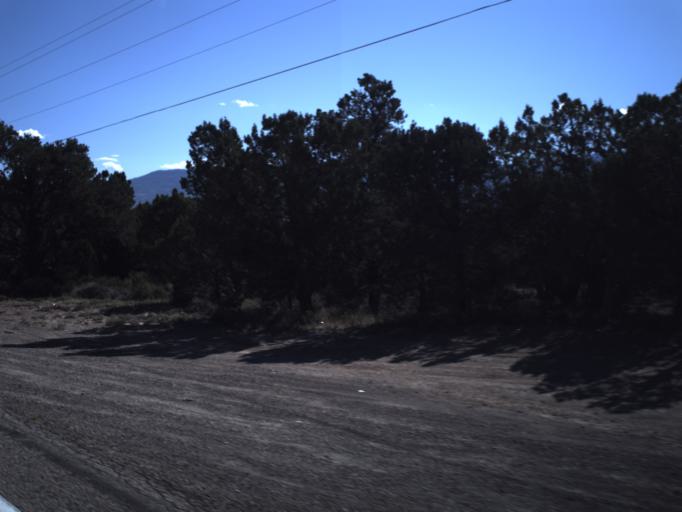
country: US
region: Utah
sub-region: Iron County
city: Cedar City
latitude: 37.6413
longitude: -113.2545
